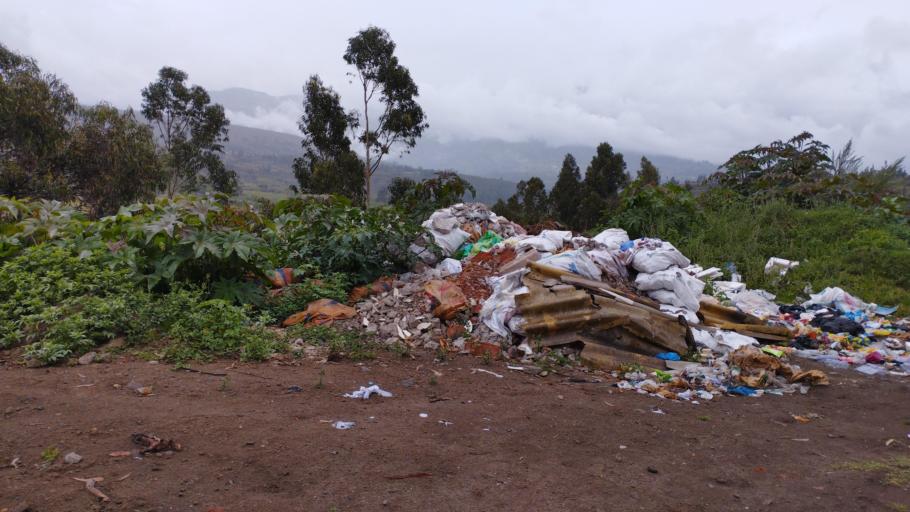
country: EC
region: Chimborazo
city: Guano
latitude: -1.6193
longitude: -78.6104
